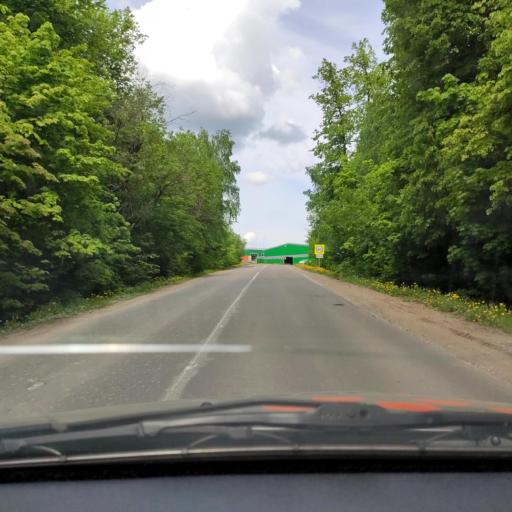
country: RU
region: Bashkortostan
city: Avdon
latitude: 54.6536
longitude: 55.7011
